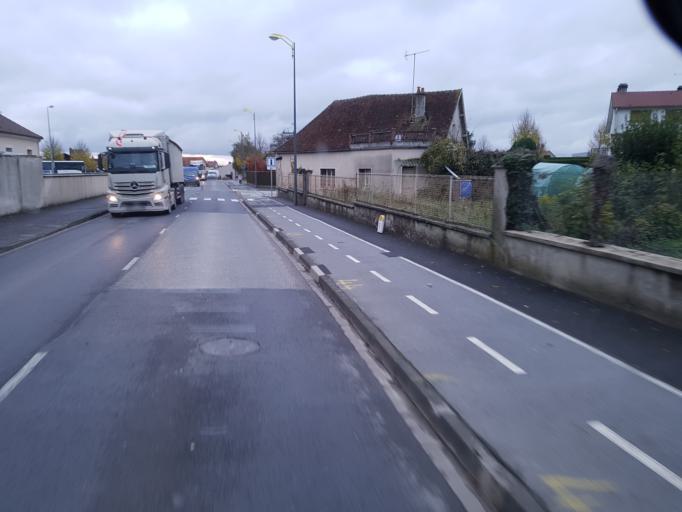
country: FR
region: Champagne-Ardenne
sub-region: Departement de la Marne
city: Montmirail
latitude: 48.8719
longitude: 3.5433
